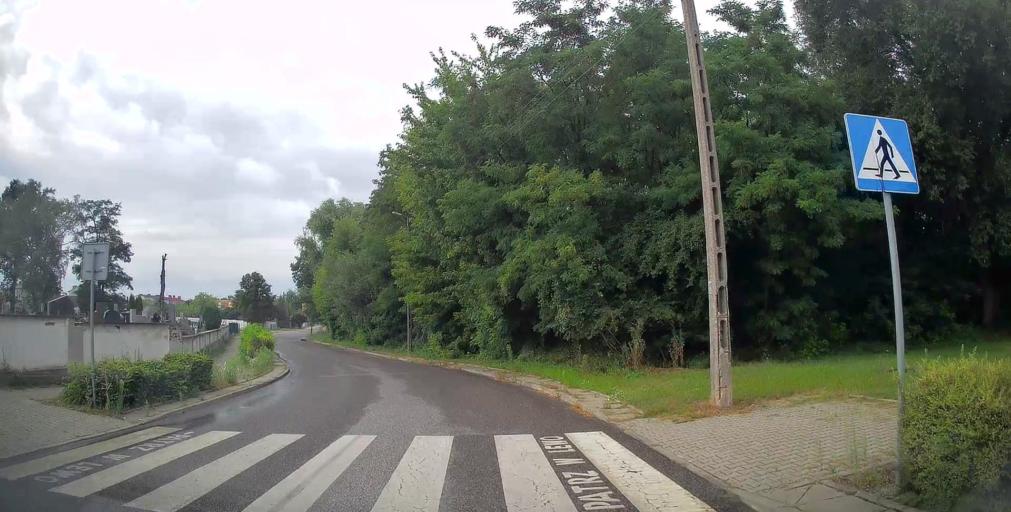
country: PL
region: Masovian Voivodeship
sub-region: Powiat bialobrzeski
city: Bialobrzegi
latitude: 51.6475
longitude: 20.9586
